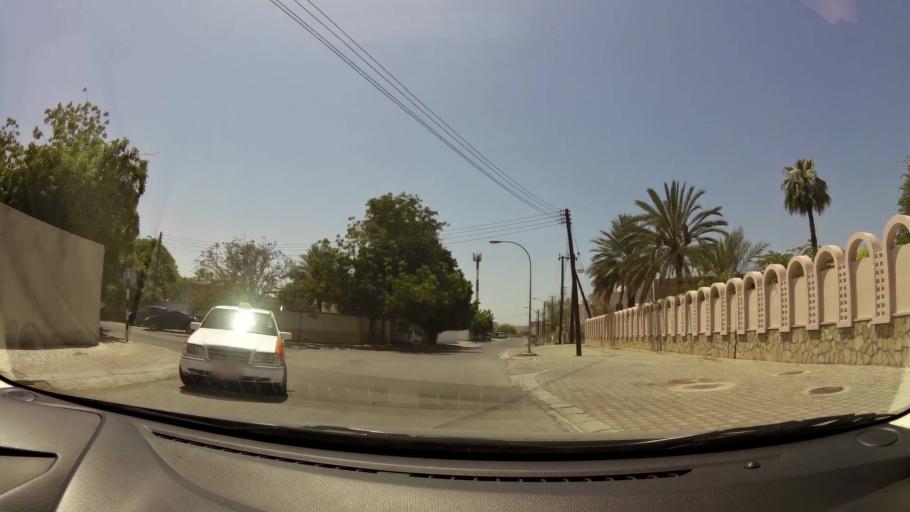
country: OM
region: Muhafazat Masqat
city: As Sib al Jadidah
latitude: 23.6294
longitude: 58.2281
